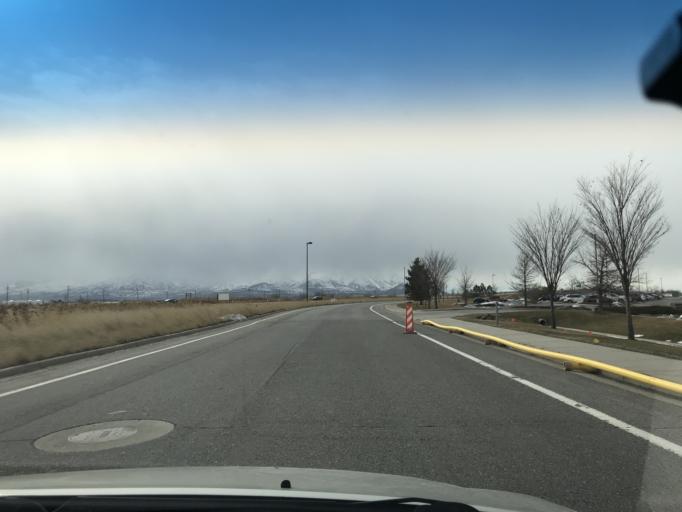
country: US
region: Utah
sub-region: Salt Lake County
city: West Valley City
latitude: 40.7721
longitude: -112.0300
